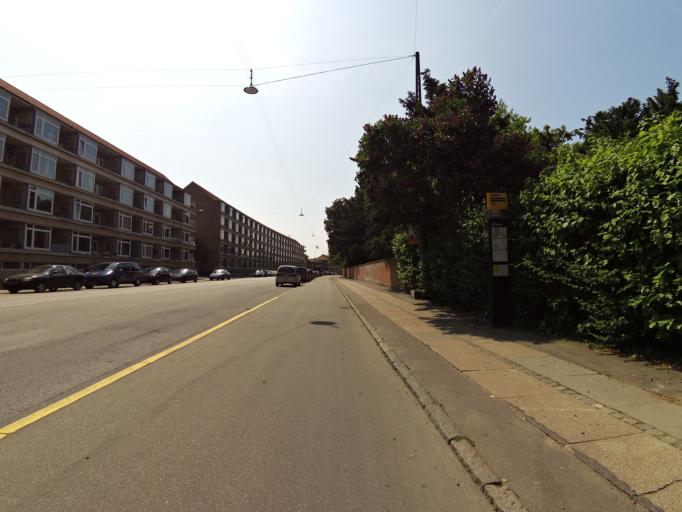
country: DK
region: Capital Region
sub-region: Frederiksberg Kommune
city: Frederiksberg
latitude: 55.7144
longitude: 12.5315
